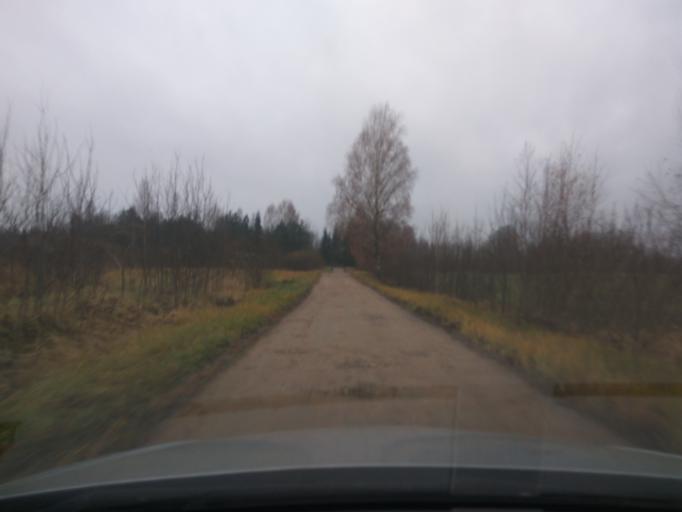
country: LV
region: Kuldigas Rajons
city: Kuldiga
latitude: 56.9336
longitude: 22.0095
